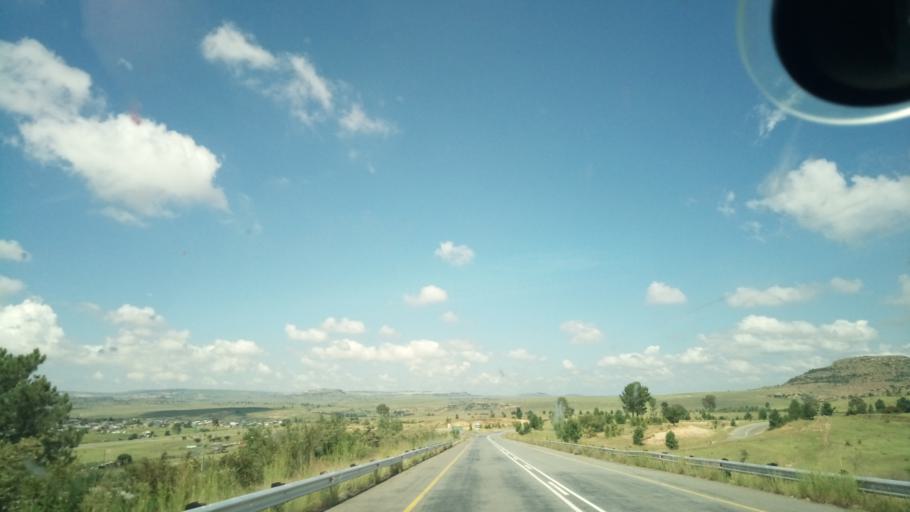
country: ZA
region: Orange Free State
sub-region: Thabo Mofutsanyana District Municipality
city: Ficksburg
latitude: -28.8860
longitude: 27.8644
